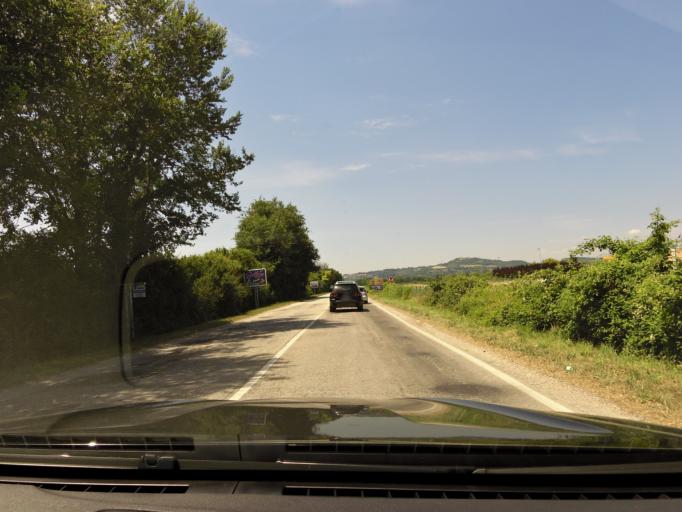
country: IT
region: The Marches
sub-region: Provincia di Pesaro e Urbino
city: Fano
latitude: 43.8203
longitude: 13.0266
